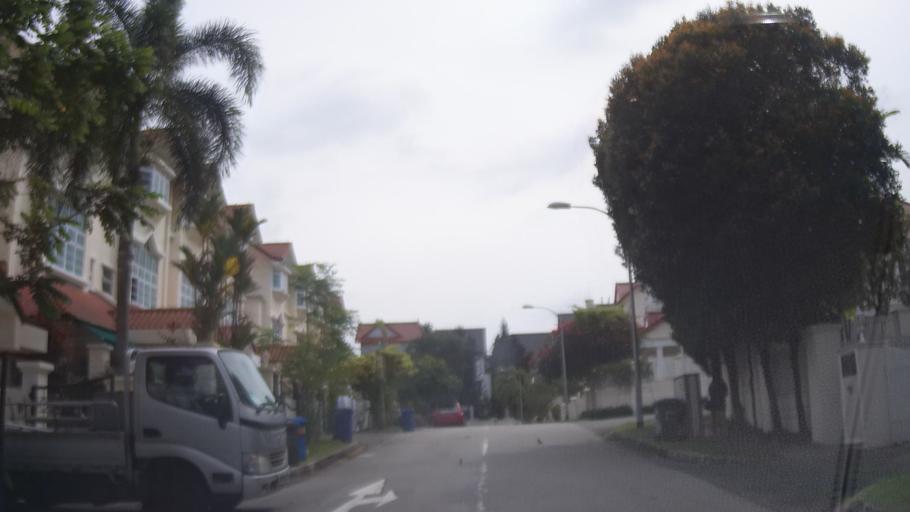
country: MY
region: Johor
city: Johor Bahru
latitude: 1.4283
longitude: 103.7782
